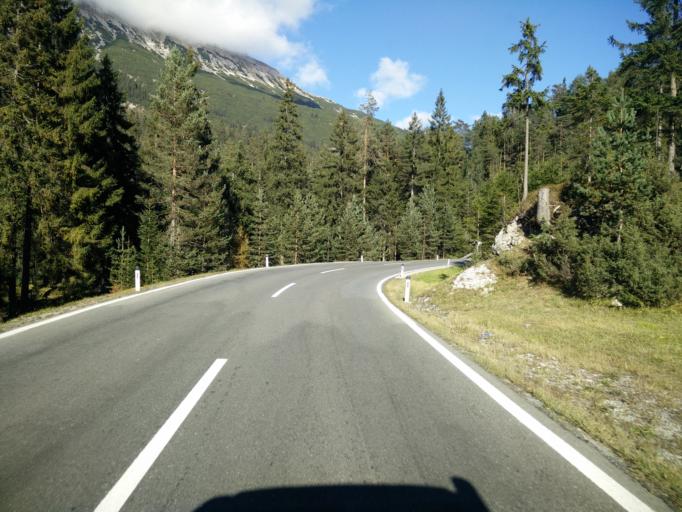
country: AT
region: Tyrol
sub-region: Politischer Bezirk Imst
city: Nassereith
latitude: 47.3601
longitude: 10.8296
